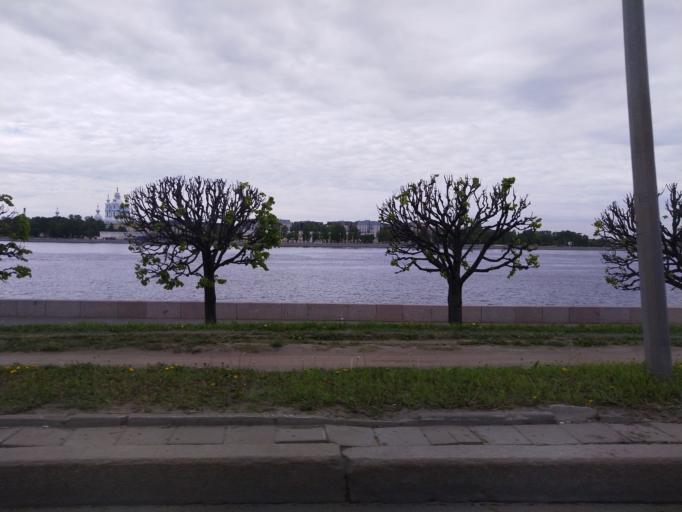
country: RU
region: Leningrad
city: Finlyandskiy
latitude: 59.9566
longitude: 30.4049
